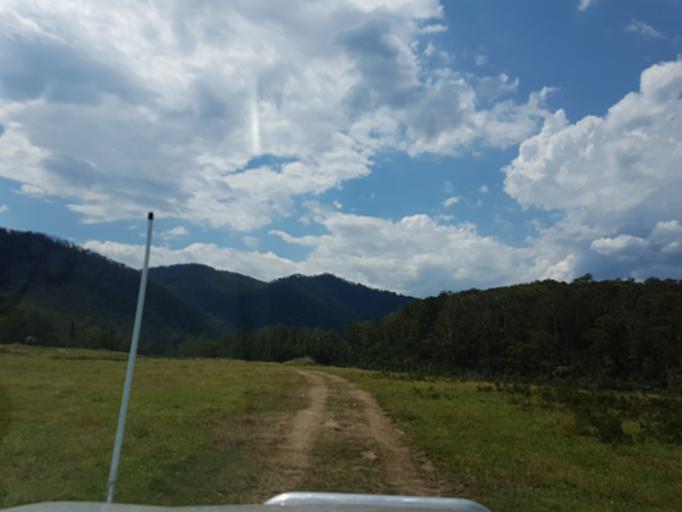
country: AU
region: Victoria
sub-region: East Gippsland
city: Lakes Entrance
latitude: -37.3994
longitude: 148.3342
